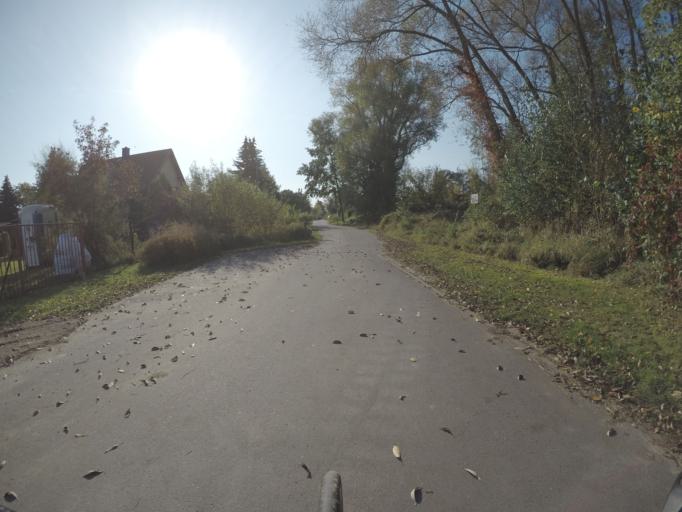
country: DE
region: Brandenburg
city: Oranienburg
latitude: 52.7355
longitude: 13.2544
